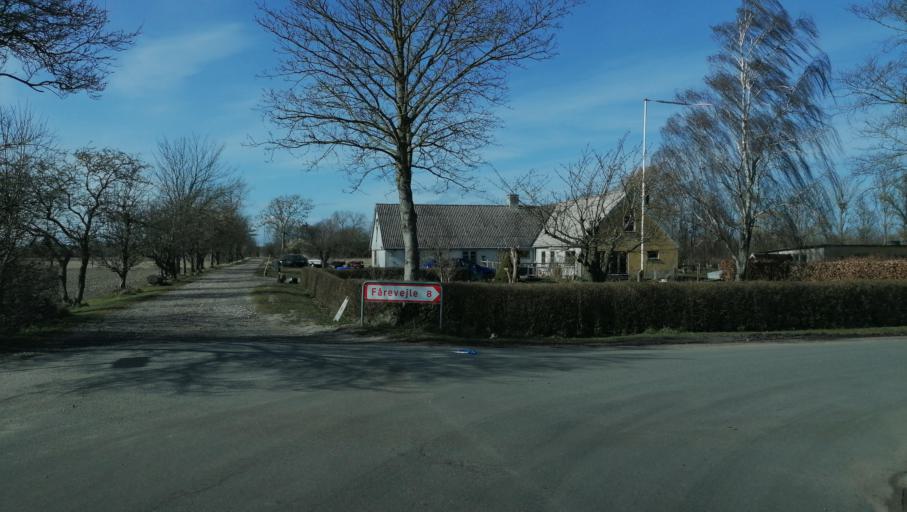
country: DK
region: Zealand
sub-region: Odsherred Kommune
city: Horve
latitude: 55.7500
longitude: 11.4801
